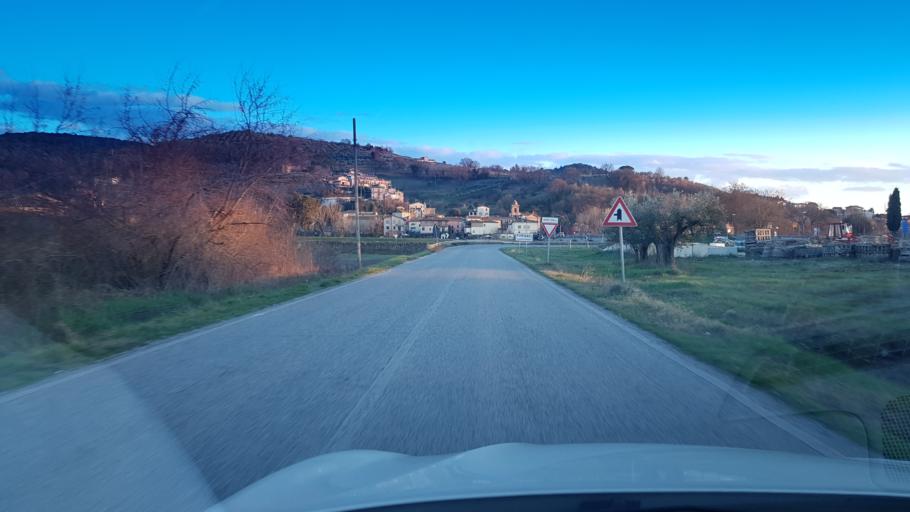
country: IT
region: Umbria
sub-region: Provincia di Perugia
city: Torgiano
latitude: 43.0132
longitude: 12.4275
